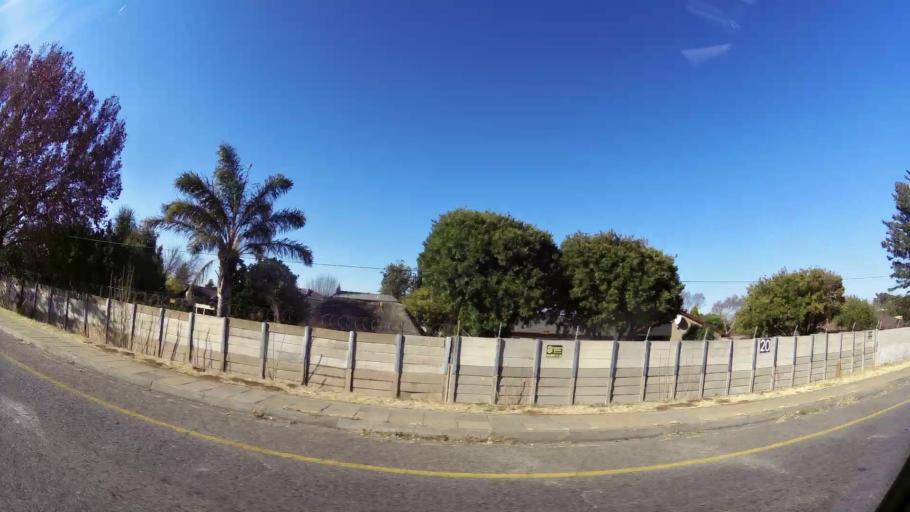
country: ZA
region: Gauteng
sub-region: Ekurhuleni Metropolitan Municipality
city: Germiston
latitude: -26.3071
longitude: 28.1083
